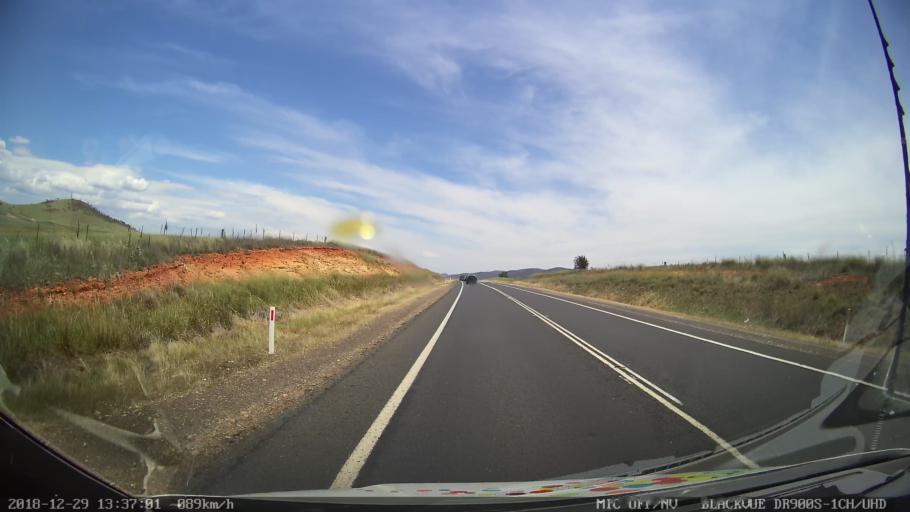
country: AU
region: New South Wales
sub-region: Cooma-Monaro
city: Cooma
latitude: -35.9778
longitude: 149.1376
